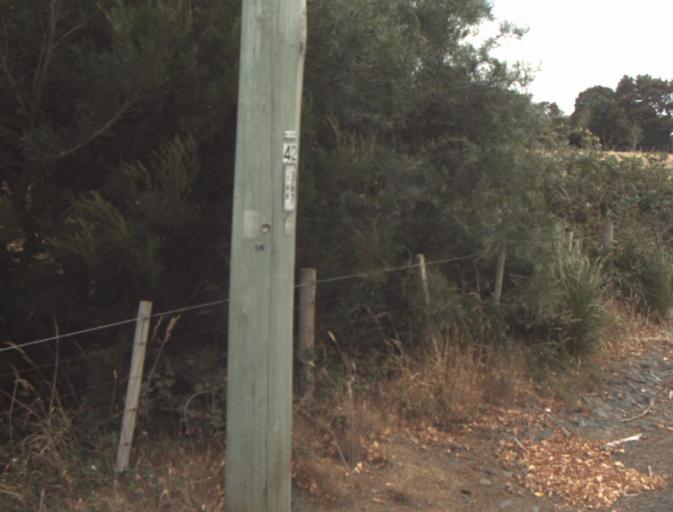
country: AU
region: Tasmania
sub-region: Launceston
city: Mayfield
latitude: -41.2926
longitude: 147.0116
